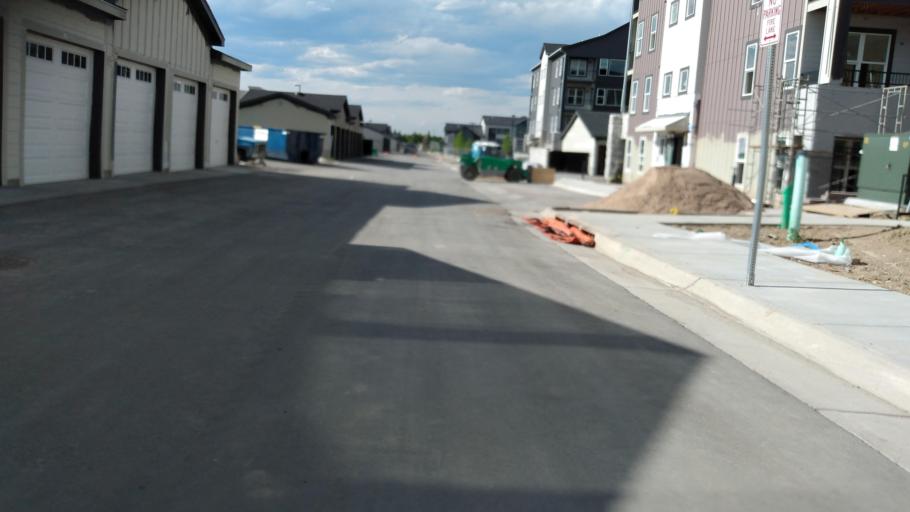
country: US
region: Colorado
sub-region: Boulder County
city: Lafayette
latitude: 40.0122
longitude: -105.0992
